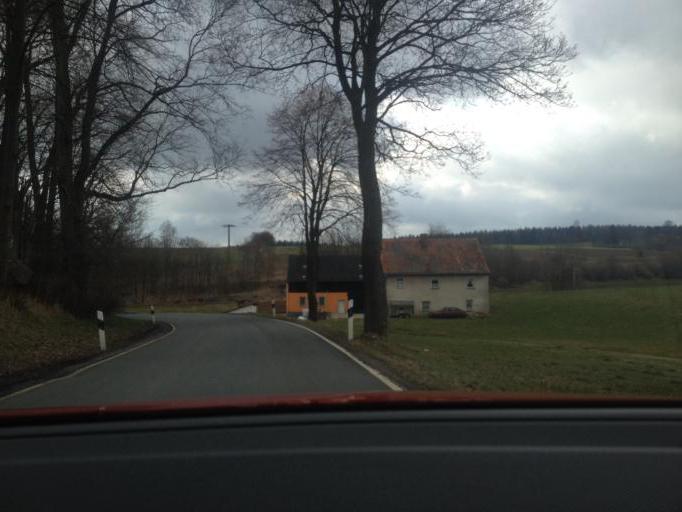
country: DE
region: Bavaria
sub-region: Upper Franconia
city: Thiersheim
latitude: 50.0723
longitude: 12.1321
